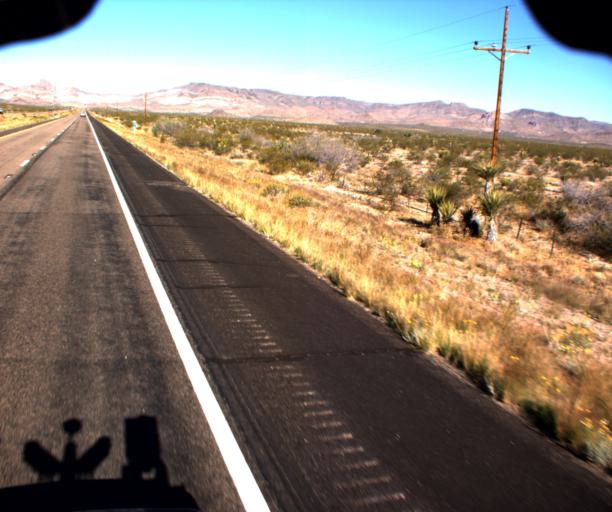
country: US
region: Arizona
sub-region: Mohave County
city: Golden Valley
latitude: 35.2271
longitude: -114.3199
